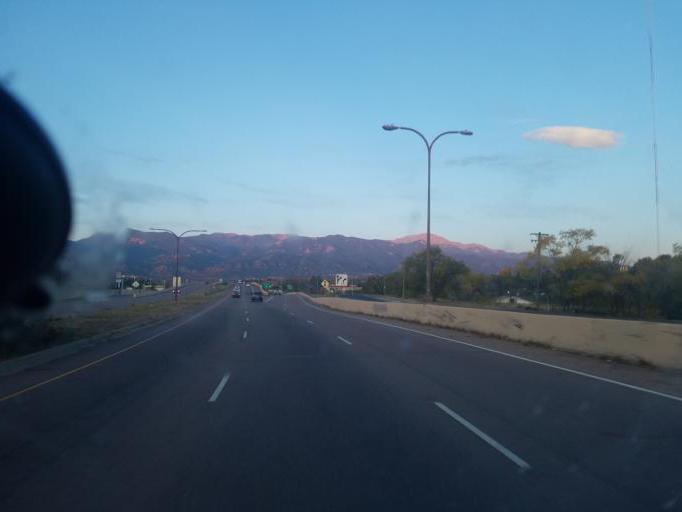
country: US
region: Colorado
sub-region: El Paso County
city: Stratmoor
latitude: 38.8181
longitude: -104.7748
